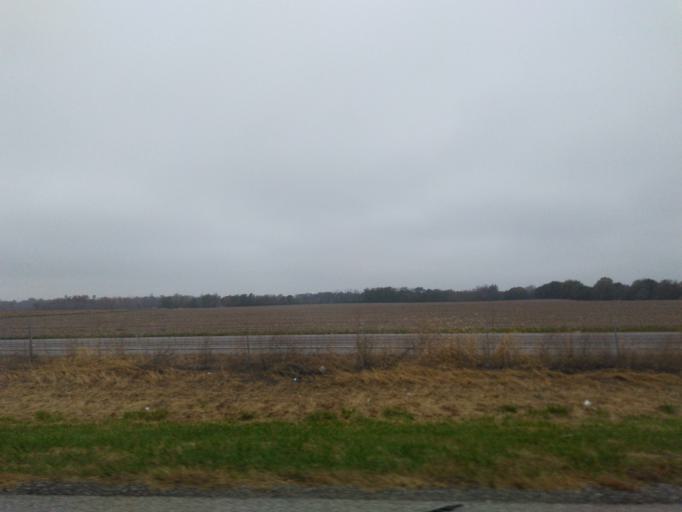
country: US
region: Illinois
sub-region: Madison County
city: Troy
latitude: 38.7220
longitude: -89.9155
